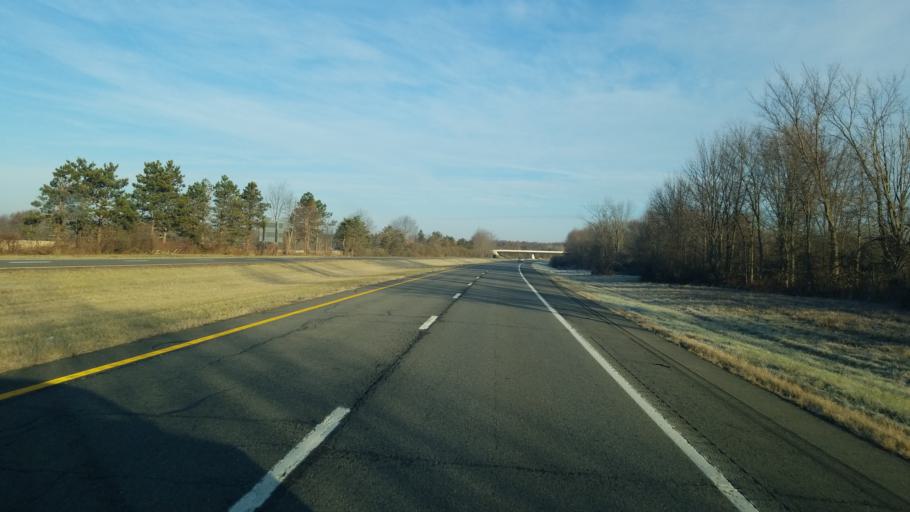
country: US
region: Ohio
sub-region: Trumbull County
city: Cortland
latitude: 41.3839
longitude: -80.7057
